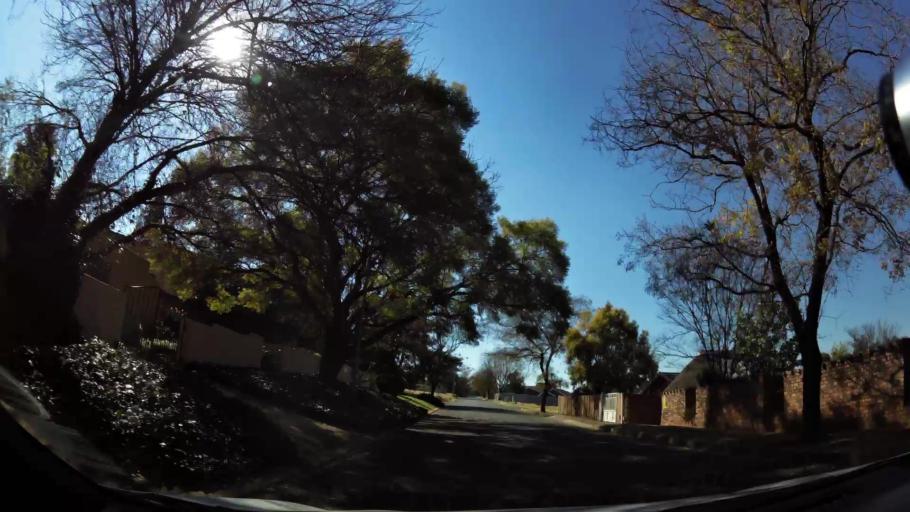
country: ZA
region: Gauteng
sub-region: City of Johannesburg Metropolitan Municipality
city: Johannesburg
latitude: -26.2761
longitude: 27.9898
